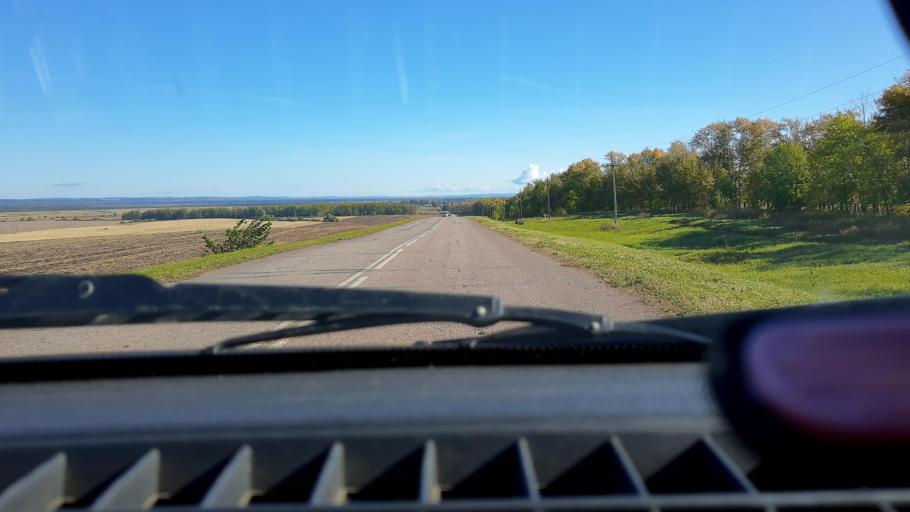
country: RU
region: Bashkortostan
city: Kushnarenkovo
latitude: 55.0756
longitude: 55.4609
